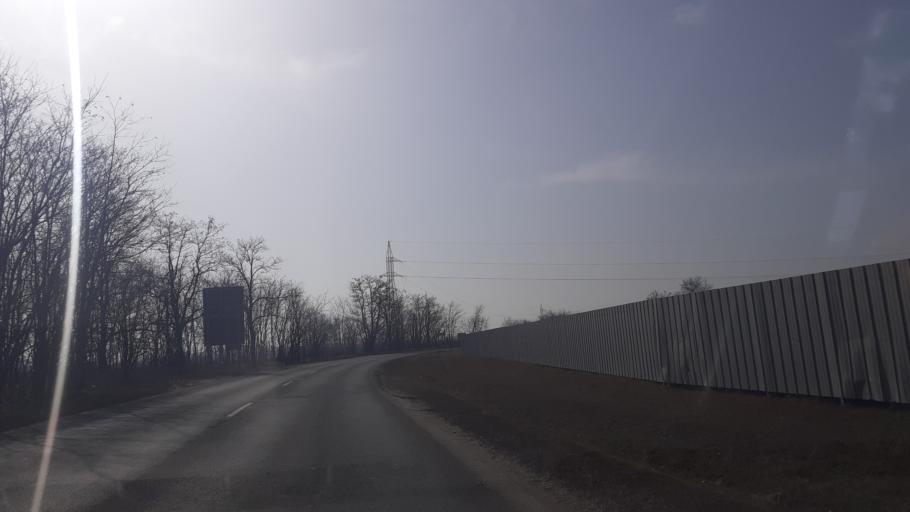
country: HU
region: Pest
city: Orkeny
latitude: 47.1454
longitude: 19.4601
